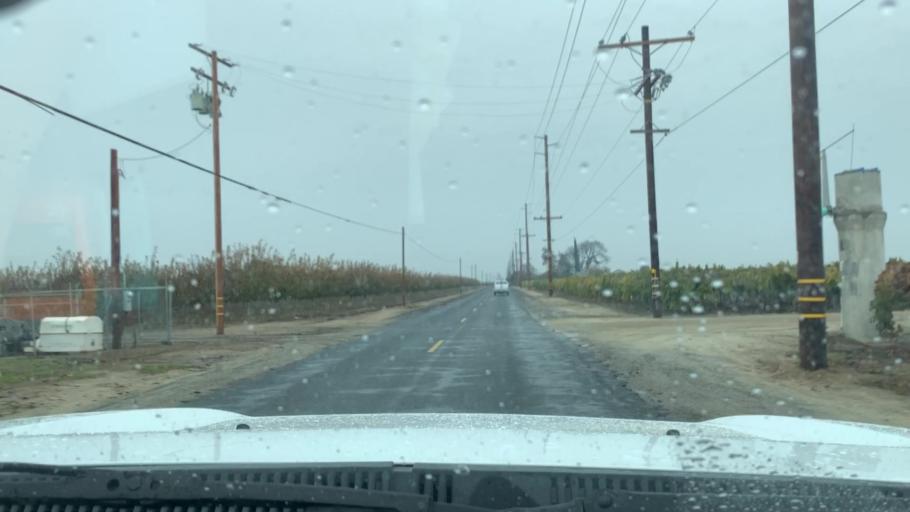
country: US
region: California
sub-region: Tulare County
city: Earlimart
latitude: 35.8339
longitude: -119.2283
